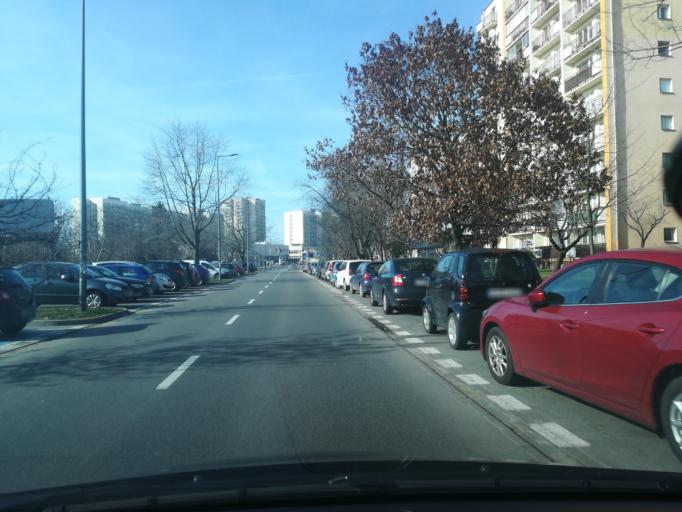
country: PL
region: Masovian Voivodeship
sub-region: Warszawa
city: Praga Poludnie
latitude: 52.2405
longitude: 21.0733
